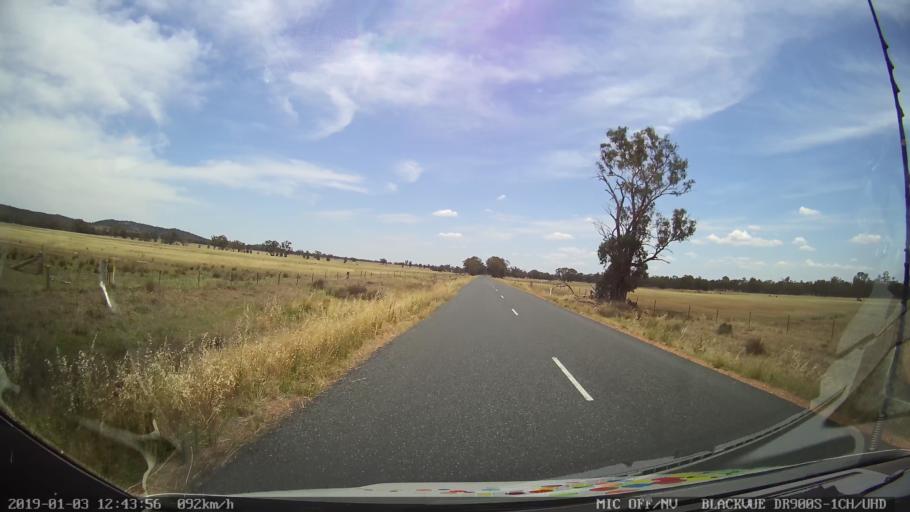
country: AU
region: New South Wales
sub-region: Weddin
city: Grenfell
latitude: -33.7681
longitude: 148.2146
